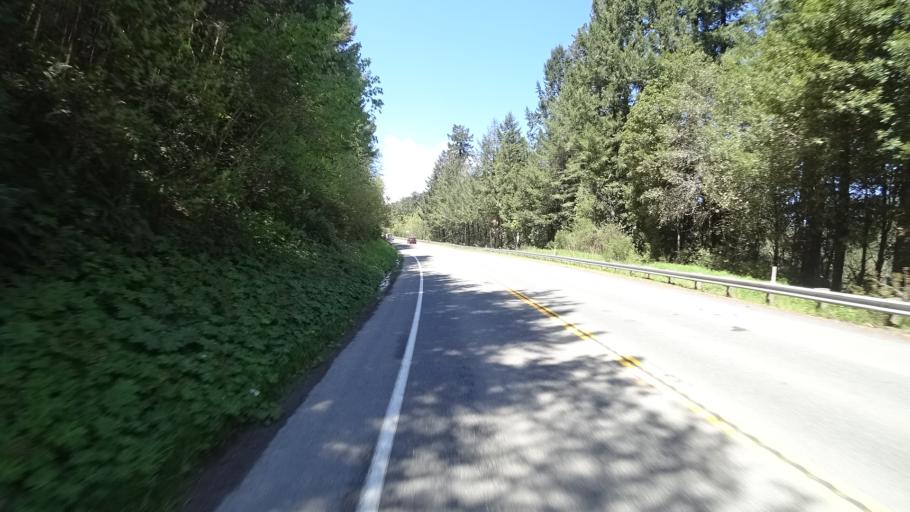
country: US
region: California
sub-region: Humboldt County
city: Blue Lake
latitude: 40.9049
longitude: -123.8122
